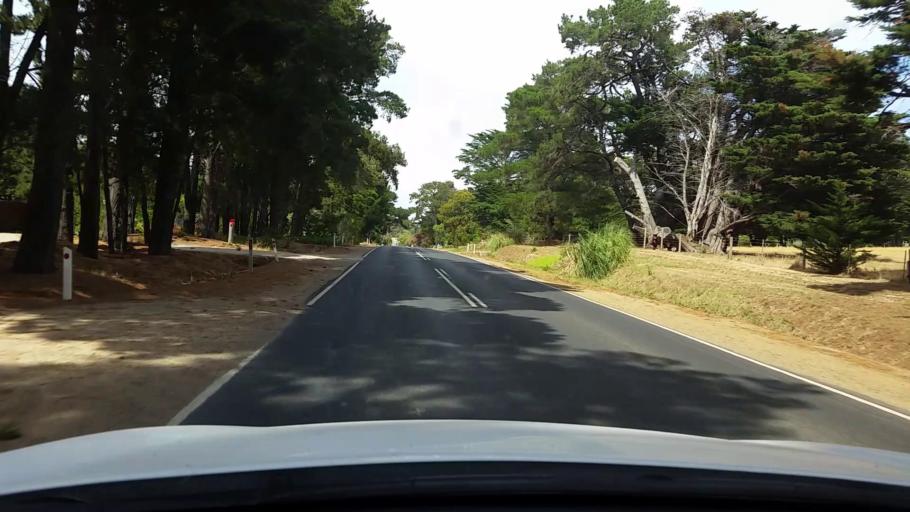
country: AU
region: Victoria
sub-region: Mornington Peninsula
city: Merricks
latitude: -38.4668
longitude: 145.0204
